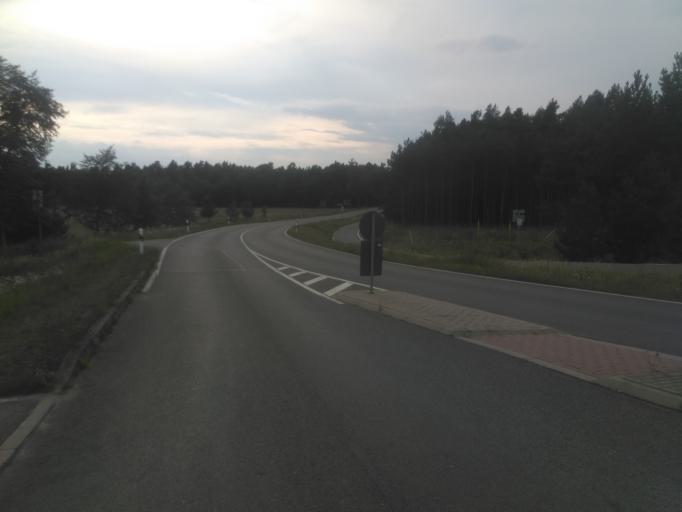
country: DE
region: Brandenburg
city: Welzow
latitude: 51.4915
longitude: 14.1454
